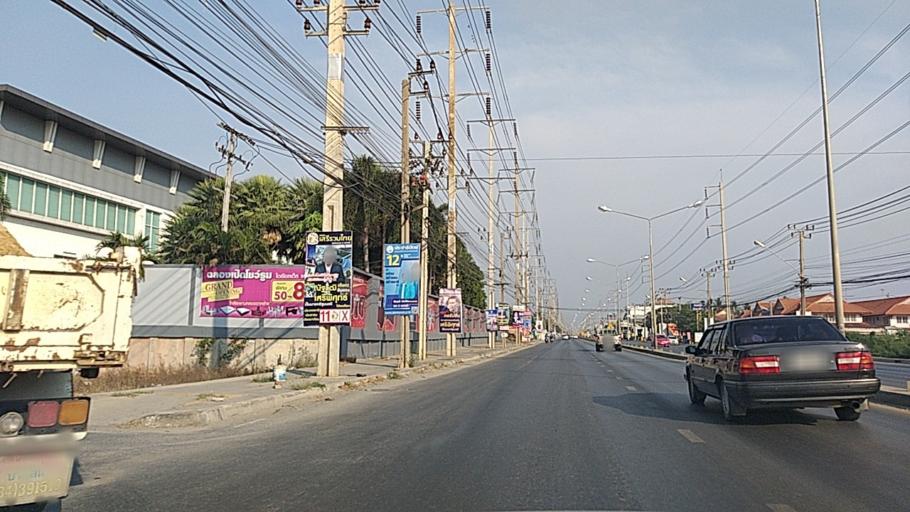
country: TH
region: Nonthaburi
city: Sai Noi
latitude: 13.9788
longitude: 100.3288
